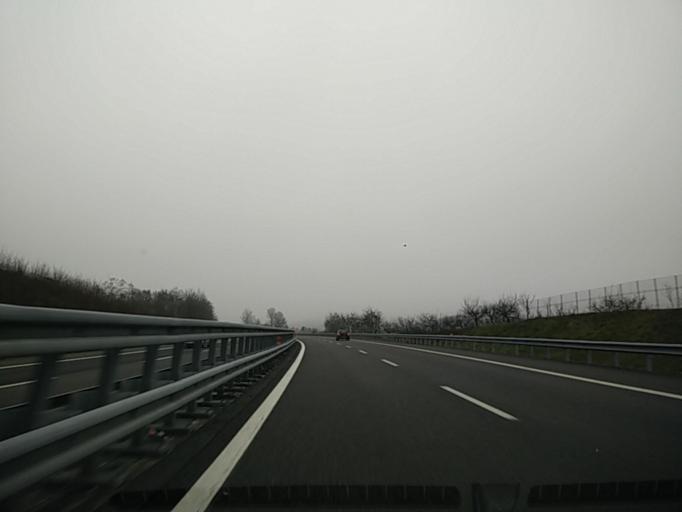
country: IT
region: Piedmont
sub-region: Provincia di Asti
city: Tigliole
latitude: 44.9026
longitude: 8.0612
